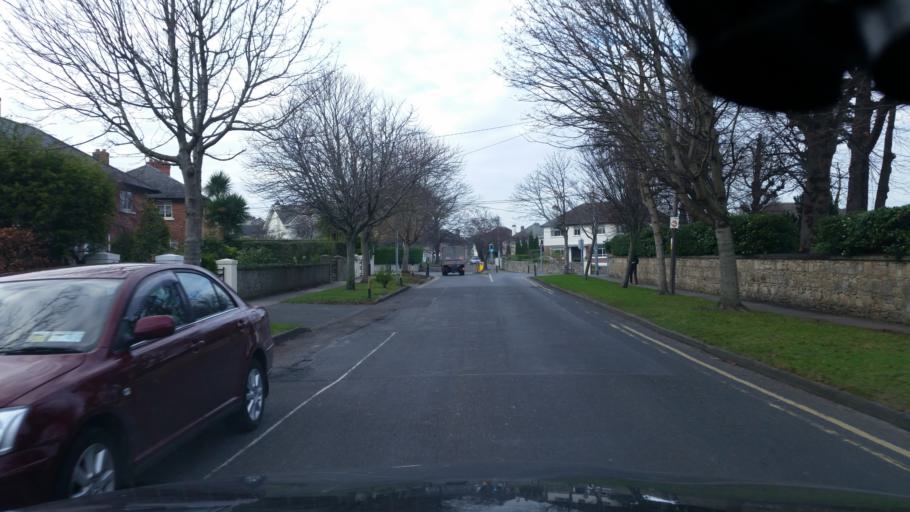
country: IE
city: Booterstown
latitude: 53.3033
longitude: -6.1979
